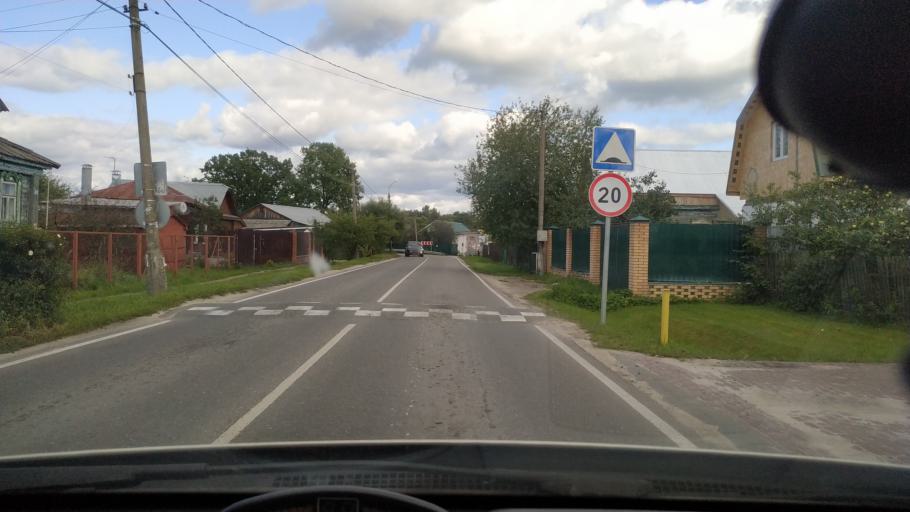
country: RU
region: Moskovskaya
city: Fryazevo
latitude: 55.7245
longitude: 38.4415
